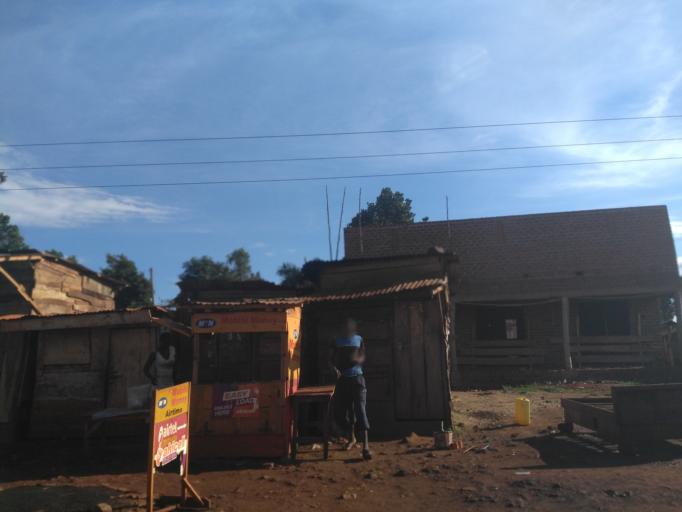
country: UG
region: Eastern Region
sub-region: Jinja District
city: Jinja
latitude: 0.4531
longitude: 33.1897
